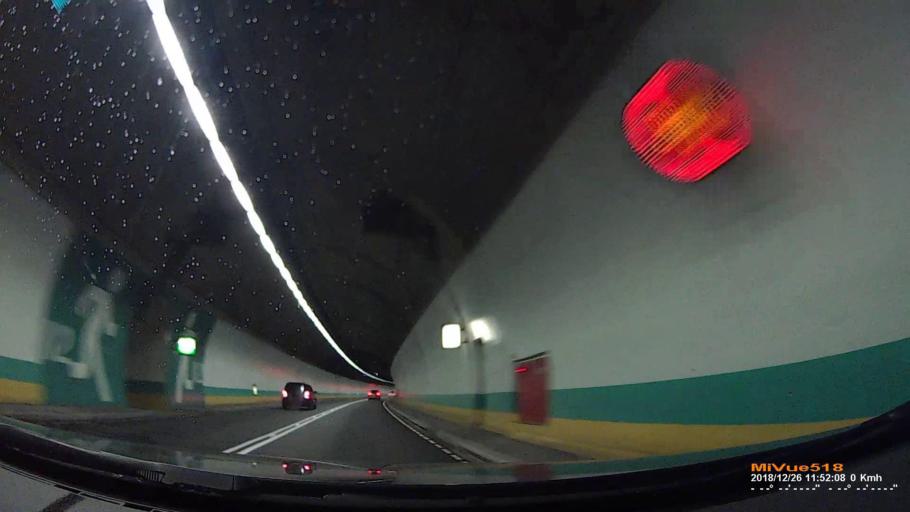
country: TW
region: Taipei
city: Taipei
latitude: 24.9693
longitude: 121.6823
